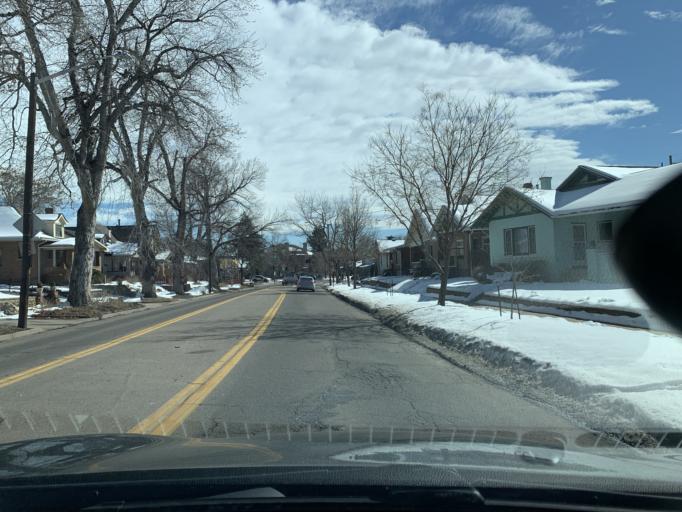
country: US
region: Colorado
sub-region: Jefferson County
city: Edgewater
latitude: 39.7630
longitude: -105.0299
